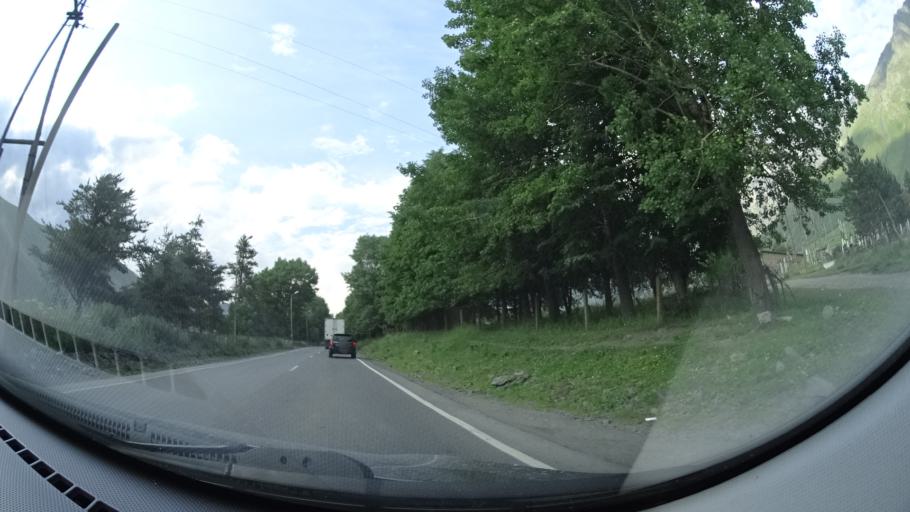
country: GE
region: Mtskheta-Mtianeti
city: Step'antsminda
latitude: 42.6477
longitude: 44.6414
